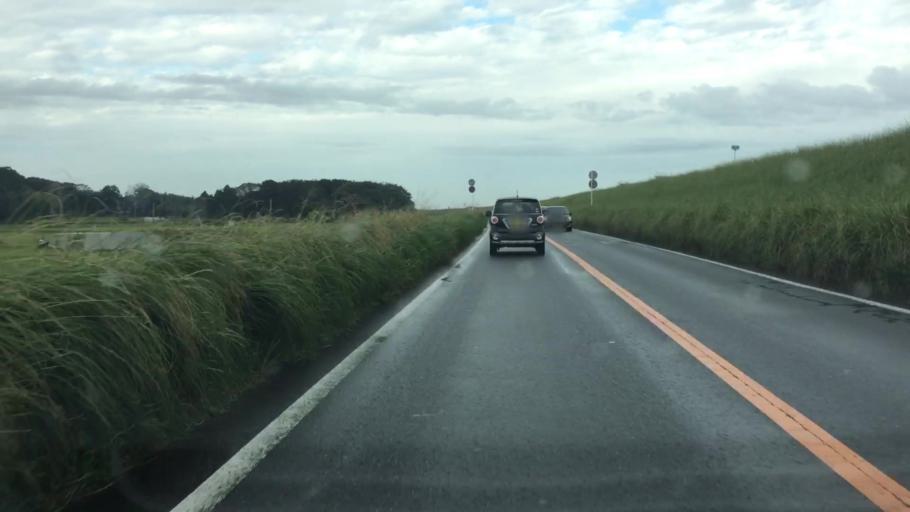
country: JP
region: Ibaraki
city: Toride
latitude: 35.8806
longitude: 140.0896
